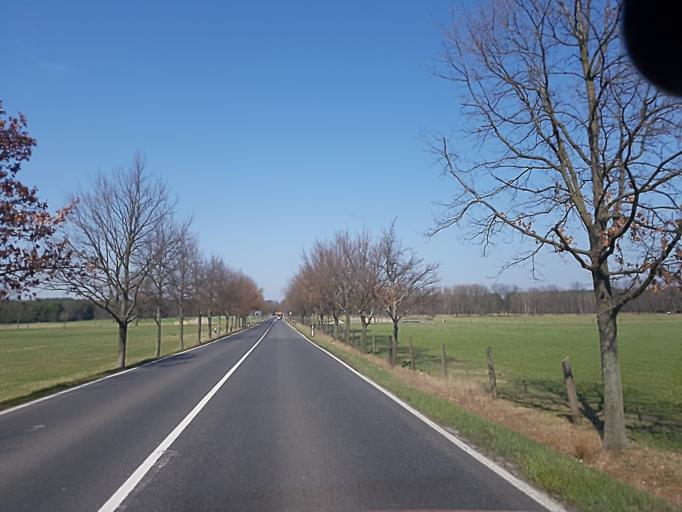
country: DE
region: Brandenburg
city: Tschernitz
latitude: 51.6522
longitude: 14.5878
